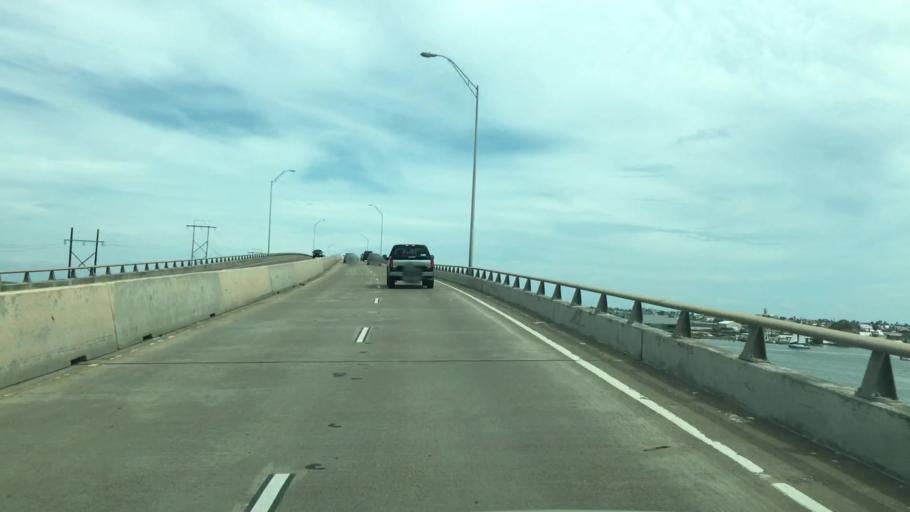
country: US
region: Texas
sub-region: Nueces County
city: Corpus Christi
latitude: 27.6363
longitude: -97.2433
